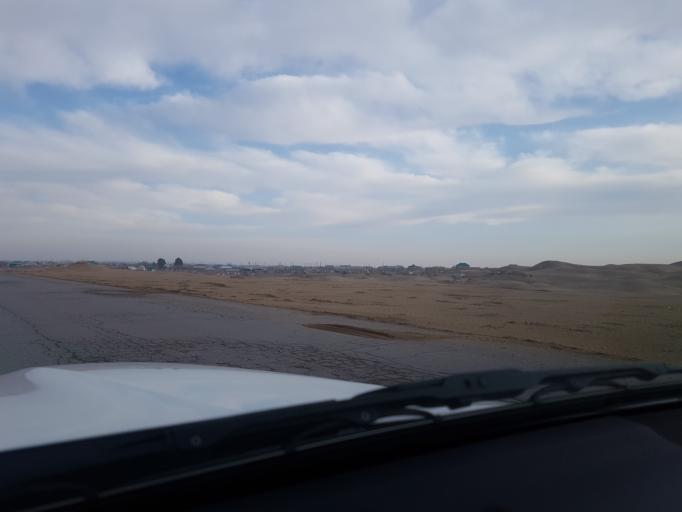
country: TM
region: Ahal
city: Abadan
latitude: 38.7467
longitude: 58.4920
